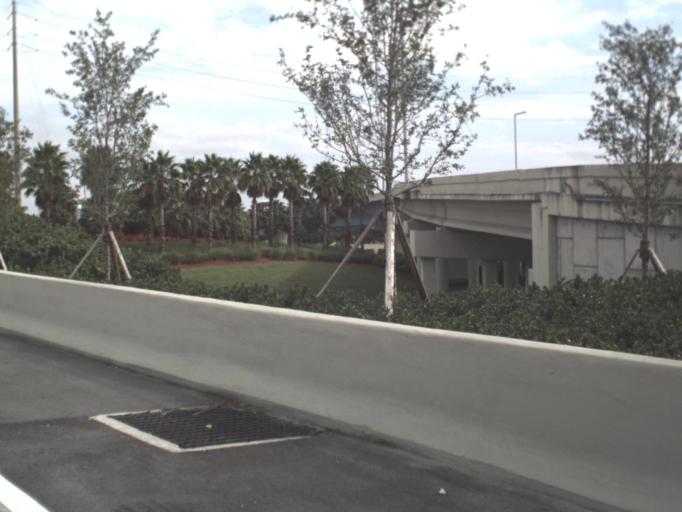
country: US
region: Florida
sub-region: Miami-Dade County
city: Miami Springs
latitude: 25.7947
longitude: -80.2663
